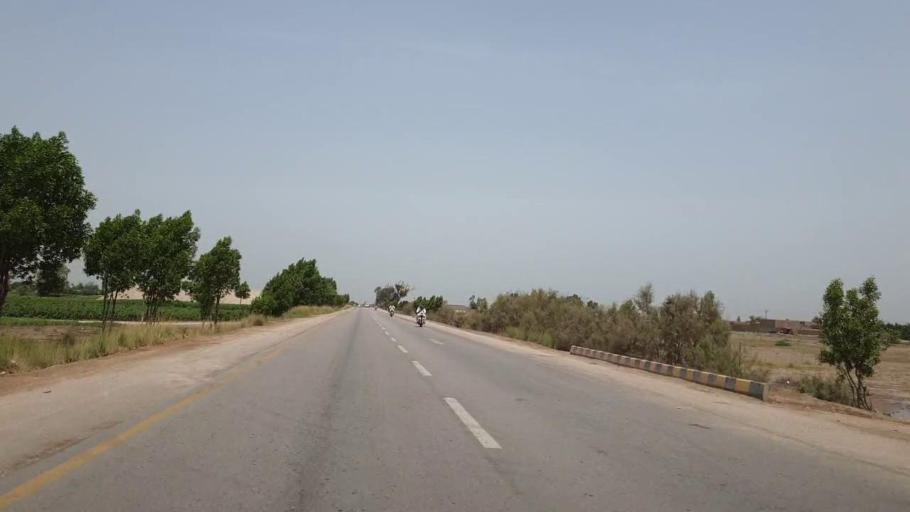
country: PK
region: Sindh
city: Nawabshah
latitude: 26.2254
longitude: 68.4930
